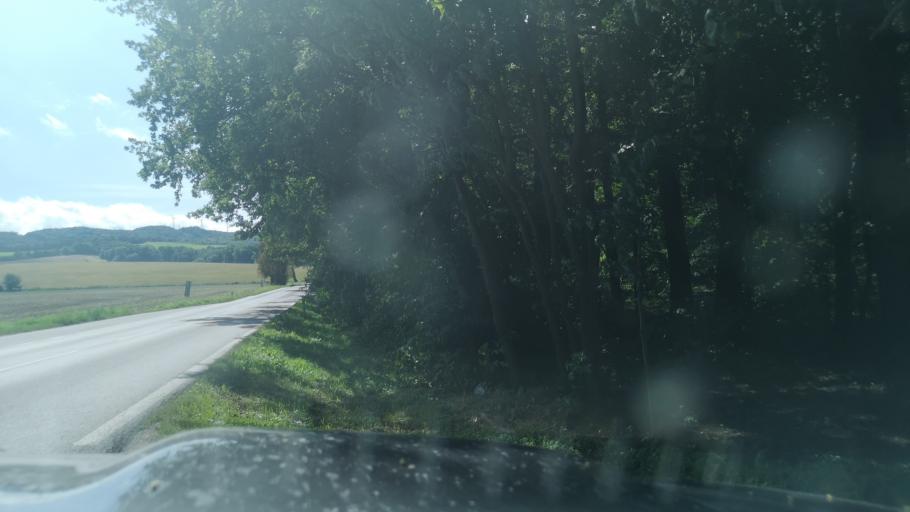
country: SK
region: Trnavsky
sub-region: Okres Senica
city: Senica
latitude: 48.5962
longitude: 17.4033
